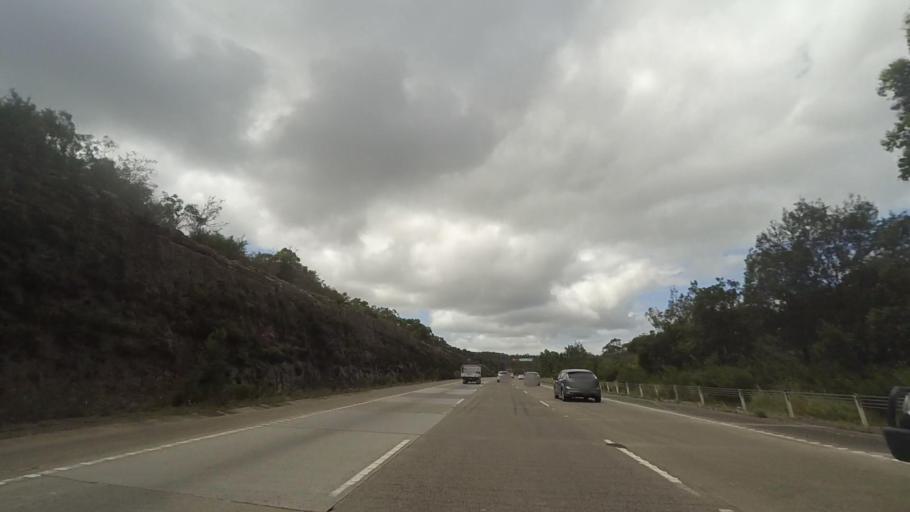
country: AU
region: New South Wales
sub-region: Gosford Shire
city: Point Clare
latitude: -33.4308
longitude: 151.2721
